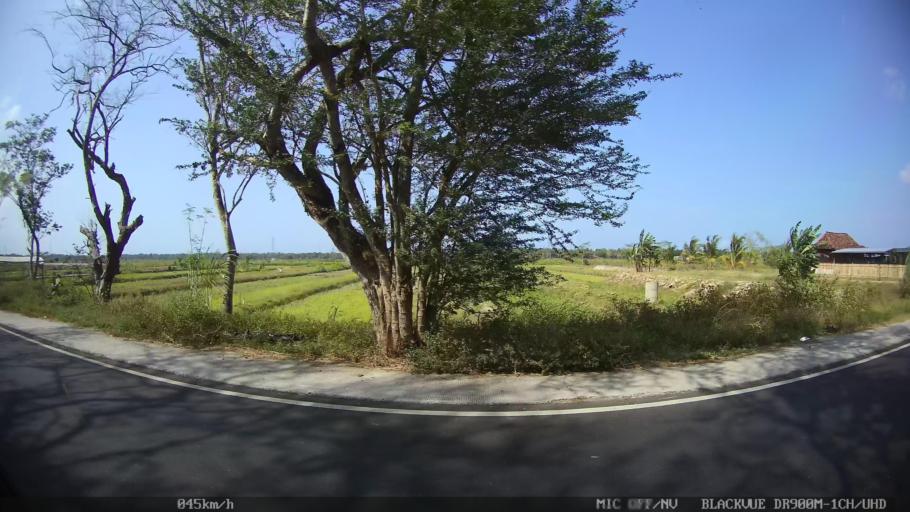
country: ID
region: Daerah Istimewa Yogyakarta
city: Srandakan
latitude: -7.8963
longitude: 110.1569
